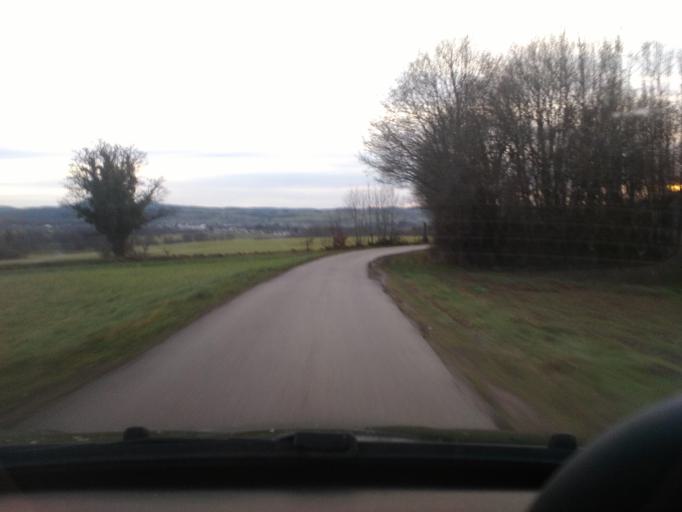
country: FR
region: Lorraine
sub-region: Departement des Vosges
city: Corcieux
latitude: 48.2048
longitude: 6.8862
